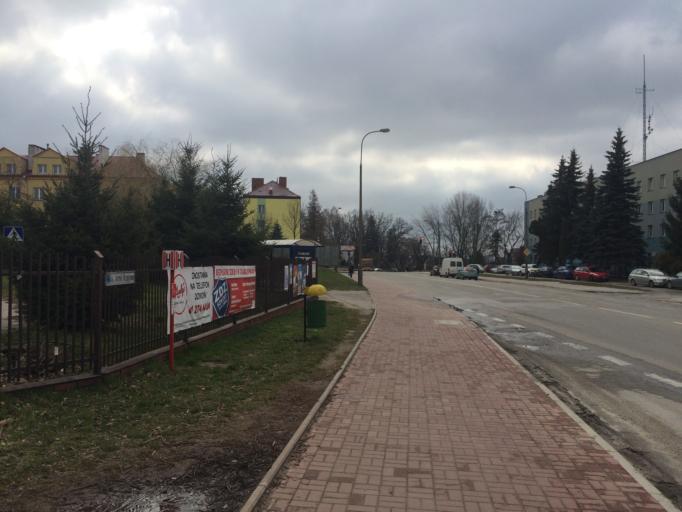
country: PL
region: Swietokrzyskie
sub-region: Powiat starachowicki
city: Starachowice
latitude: 51.0532
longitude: 21.0744
